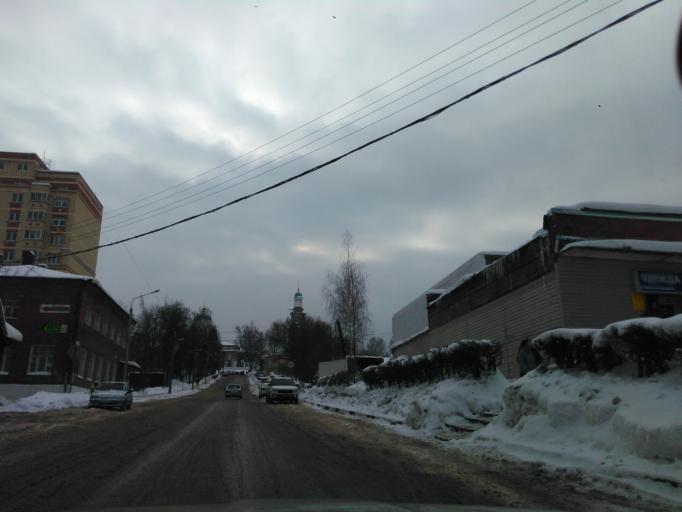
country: RU
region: Moskovskaya
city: Yakhroma
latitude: 56.2885
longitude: 37.4827
